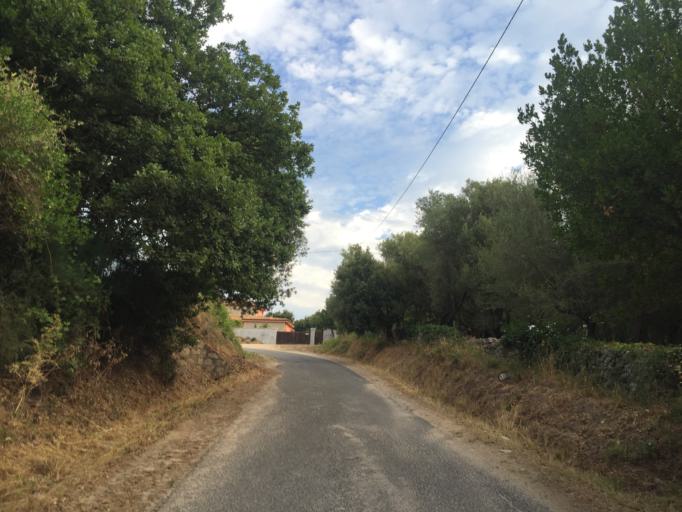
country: IT
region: Sardinia
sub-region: Provincia di Olbia-Tempio
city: Aggius
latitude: 40.9274
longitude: 9.0710
